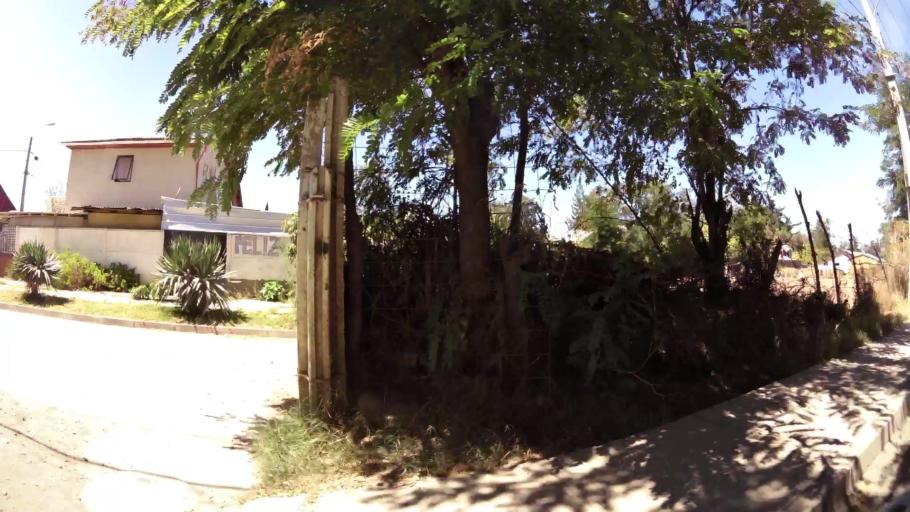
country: CL
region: O'Higgins
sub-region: Provincia de Cachapoal
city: Rancagua
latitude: -34.1460
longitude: -70.7230
